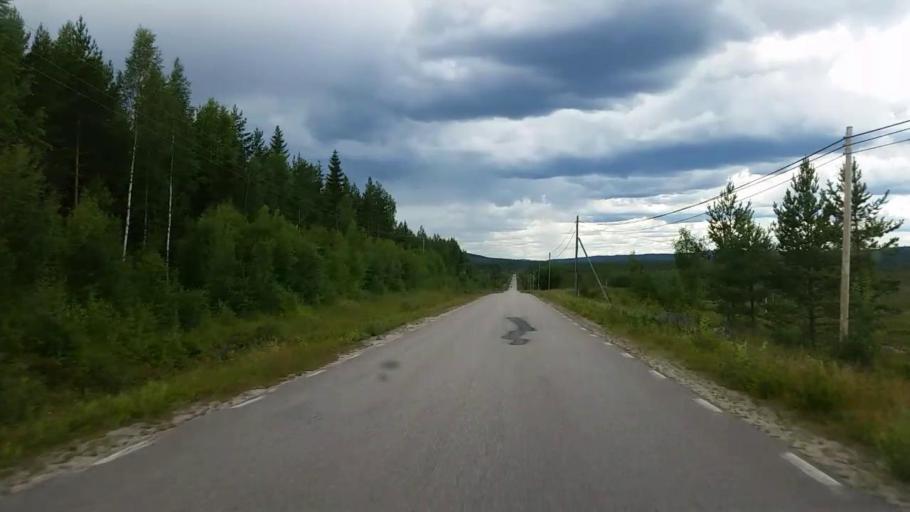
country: SE
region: Gaevleborg
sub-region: Ovanakers Kommun
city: Edsbyn
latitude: 61.4366
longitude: 15.8947
